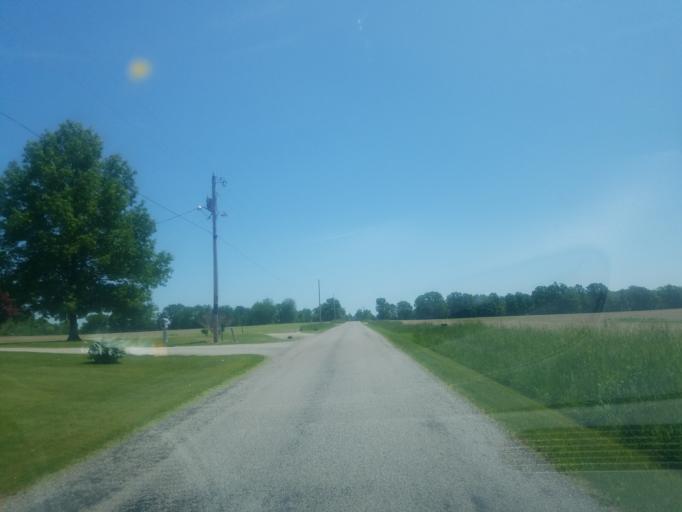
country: US
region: Ohio
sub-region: Huron County
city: New London
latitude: 41.1379
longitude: -82.3662
